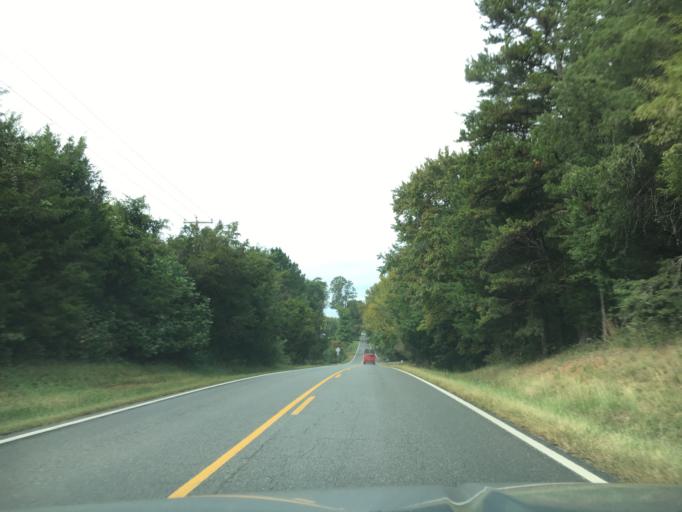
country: US
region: Virginia
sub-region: Goochland County
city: Goochland
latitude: 37.7448
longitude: -77.8510
